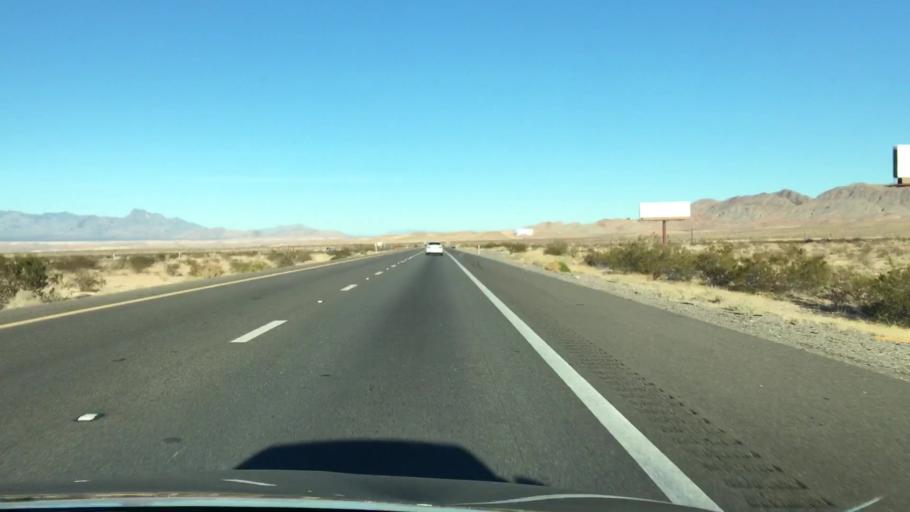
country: US
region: Nevada
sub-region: Clark County
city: Moapa Town
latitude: 36.5742
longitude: -114.6647
